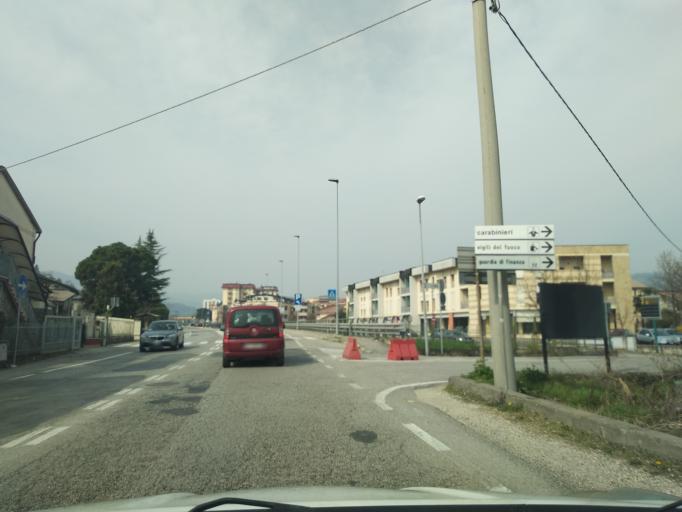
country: IT
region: Veneto
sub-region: Provincia di Vicenza
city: Arzignano
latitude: 45.5160
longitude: 11.3376
